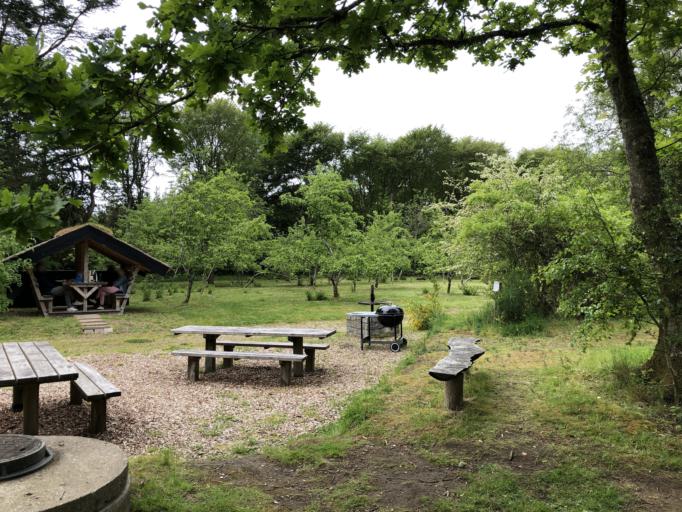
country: DK
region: Central Jutland
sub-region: Holstebro Kommune
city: Ulfborg
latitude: 56.2796
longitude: 8.1701
